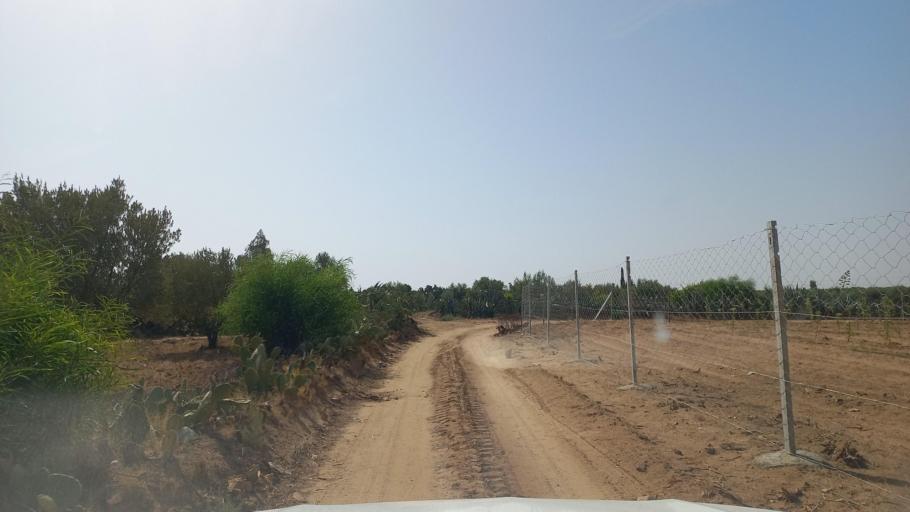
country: TN
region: Al Qasrayn
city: Kasserine
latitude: 35.2404
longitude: 9.0504
